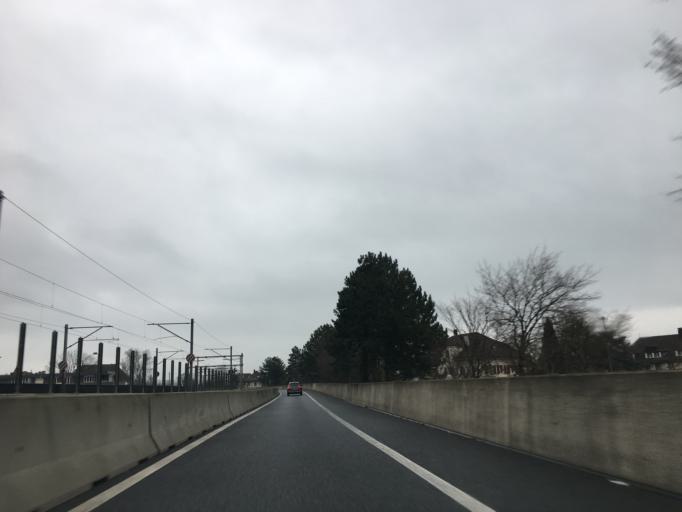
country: CH
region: Bern
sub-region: Jura bernois
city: La Neuveville
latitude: 47.0614
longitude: 7.0883
